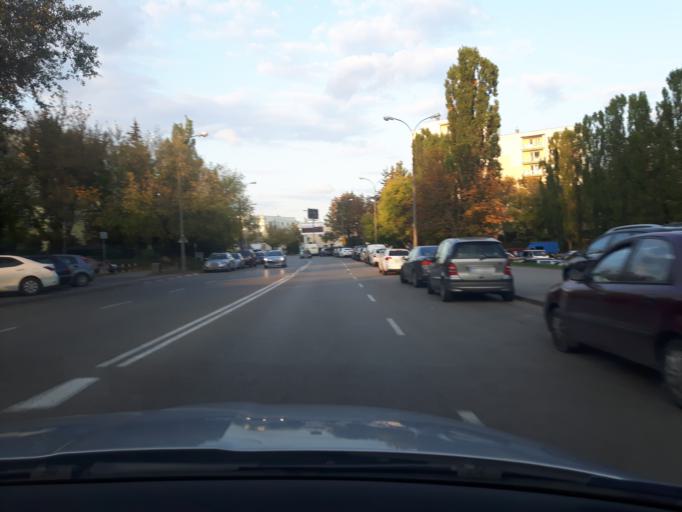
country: PL
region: Masovian Voivodeship
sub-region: Warszawa
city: Ursynow
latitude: 52.1570
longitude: 21.0360
